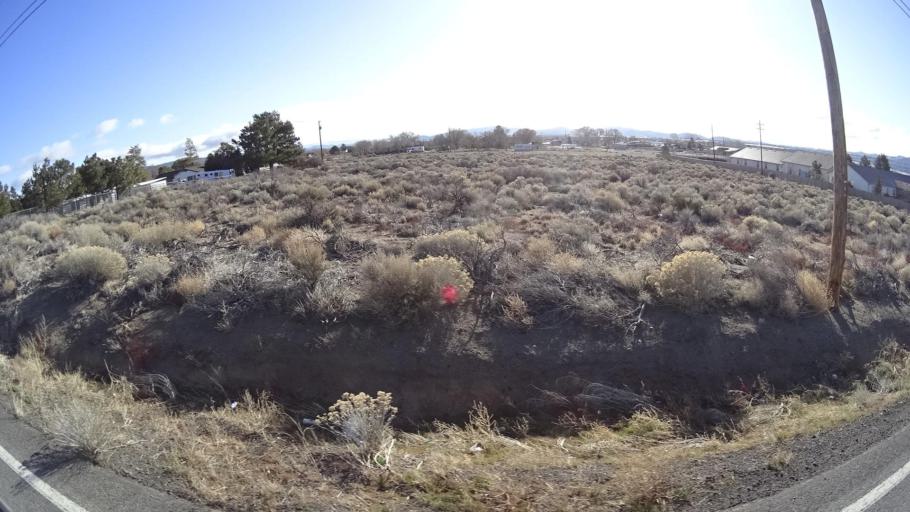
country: US
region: Nevada
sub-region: Washoe County
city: Cold Springs
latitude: 39.6584
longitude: -119.9224
